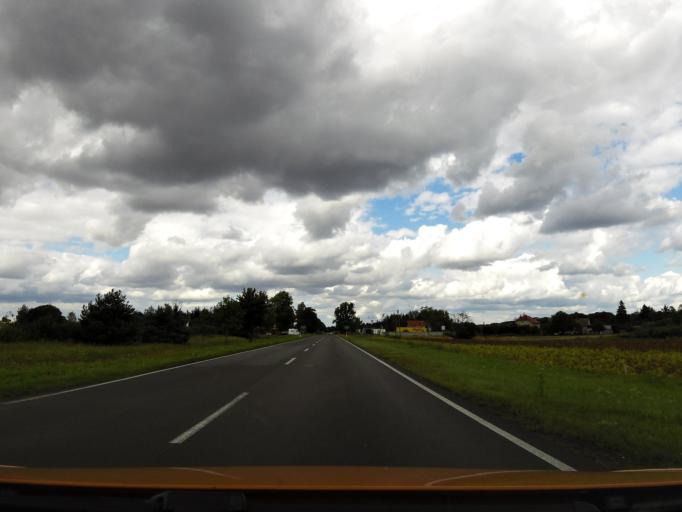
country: PL
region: West Pomeranian Voivodeship
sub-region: Powiat gryficki
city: Ploty
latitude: 53.7894
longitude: 15.2527
